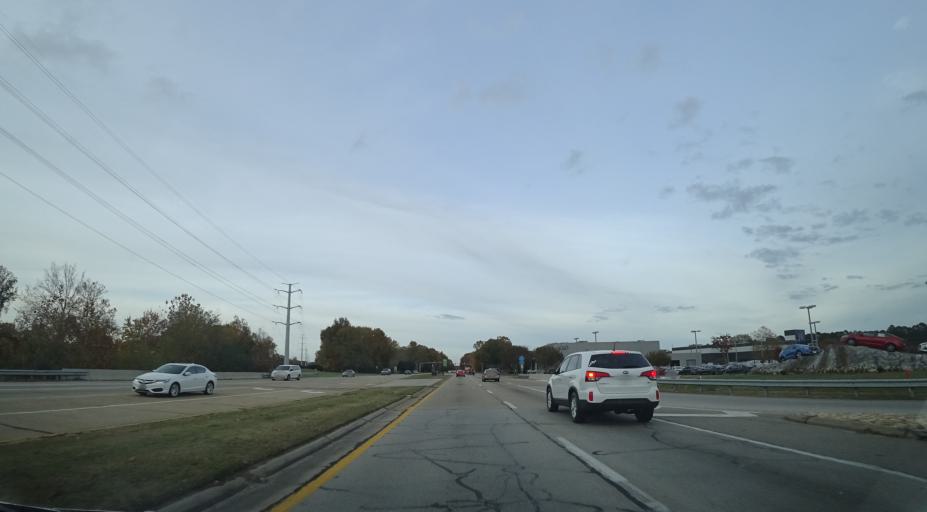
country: US
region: Virginia
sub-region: City of Hampton
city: Hampton
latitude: 37.0607
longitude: -76.4010
